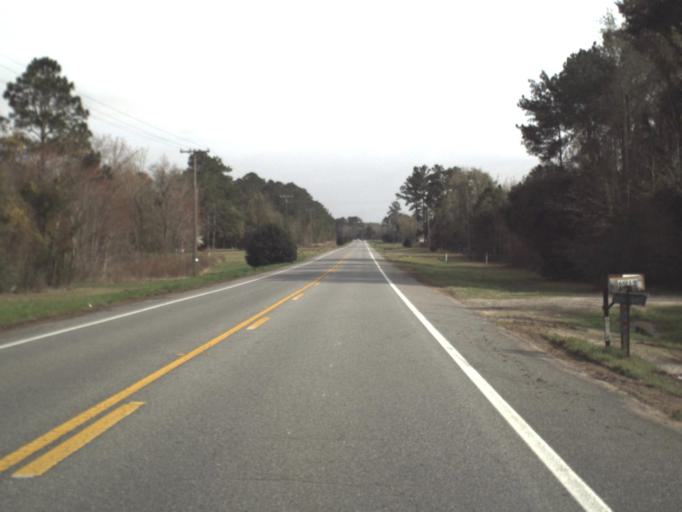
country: US
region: Florida
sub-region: Jefferson County
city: Monticello
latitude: 30.5144
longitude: -83.7792
